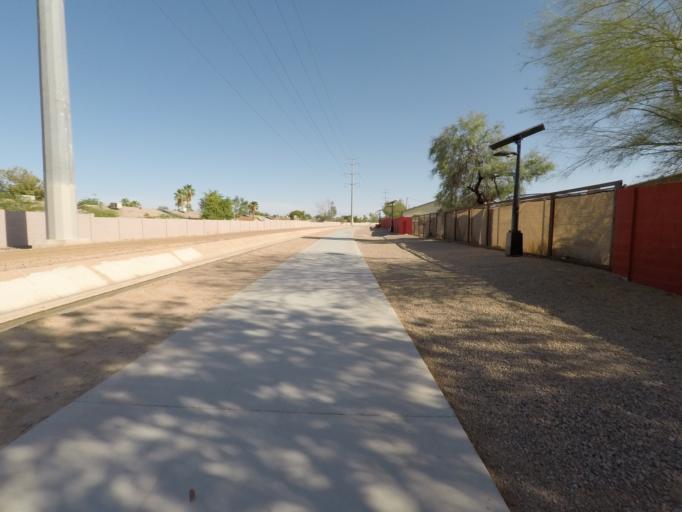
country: US
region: Arizona
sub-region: Maricopa County
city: Guadalupe
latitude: 33.3681
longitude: -111.9575
